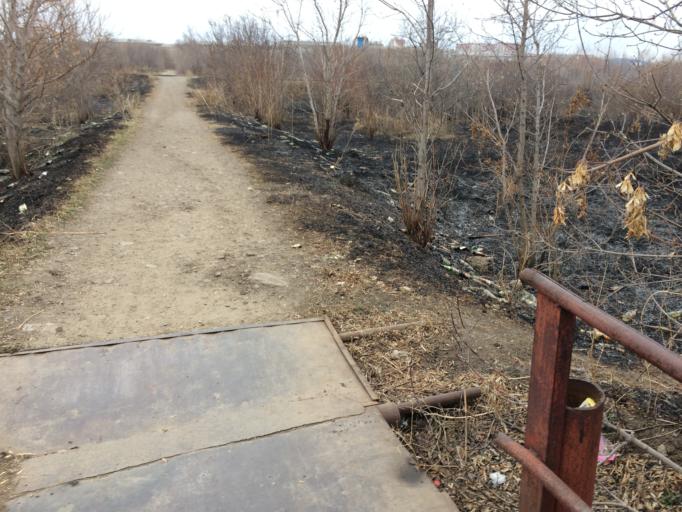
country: RU
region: Chelyabinsk
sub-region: Gorod Magnitogorsk
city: Magnitogorsk
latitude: 53.4423
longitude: 58.9763
